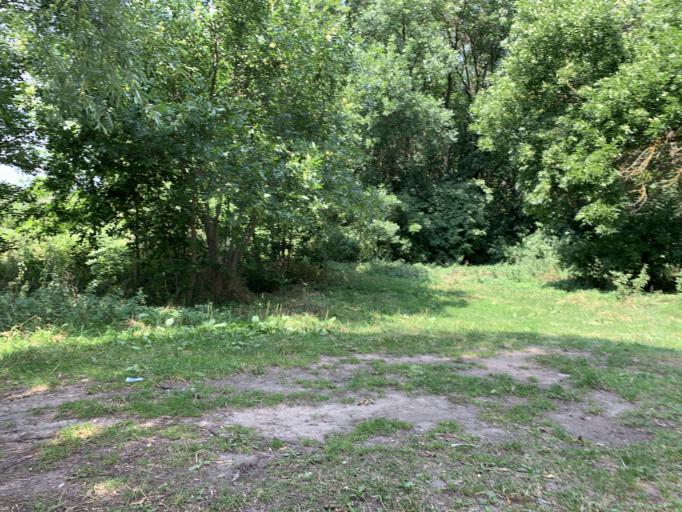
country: BY
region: Minsk
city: Nyasvizh
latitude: 53.2316
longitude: 26.7040
